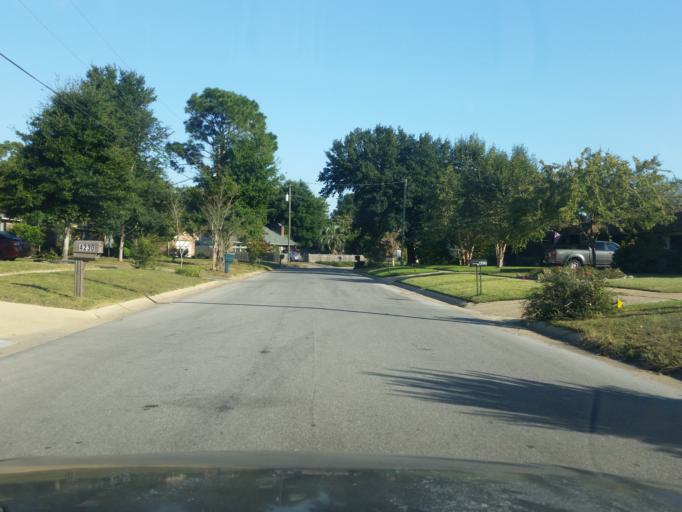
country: US
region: Florida
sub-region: Escambia County
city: Ferry Pass
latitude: 30.4921
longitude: -87.1688
